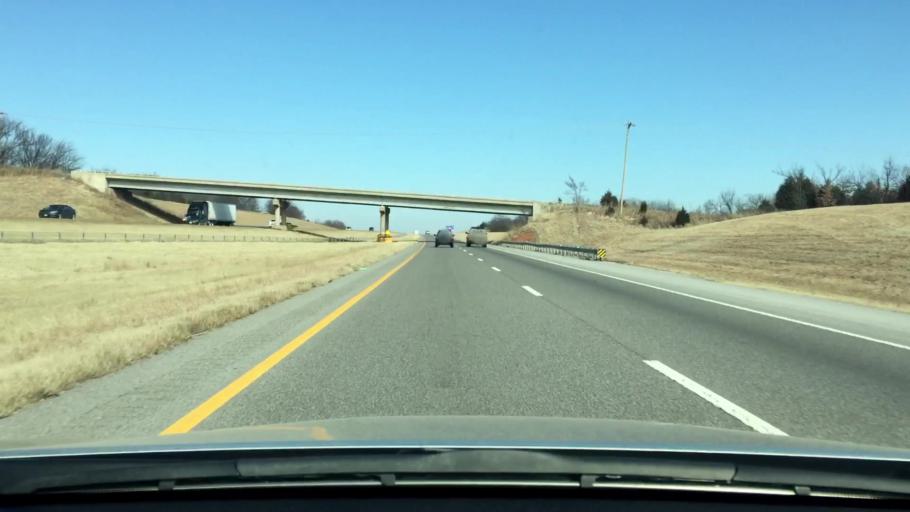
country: US
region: Oklahoma
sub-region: McClain County
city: Purcell
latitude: 34.9559
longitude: -97.3687
